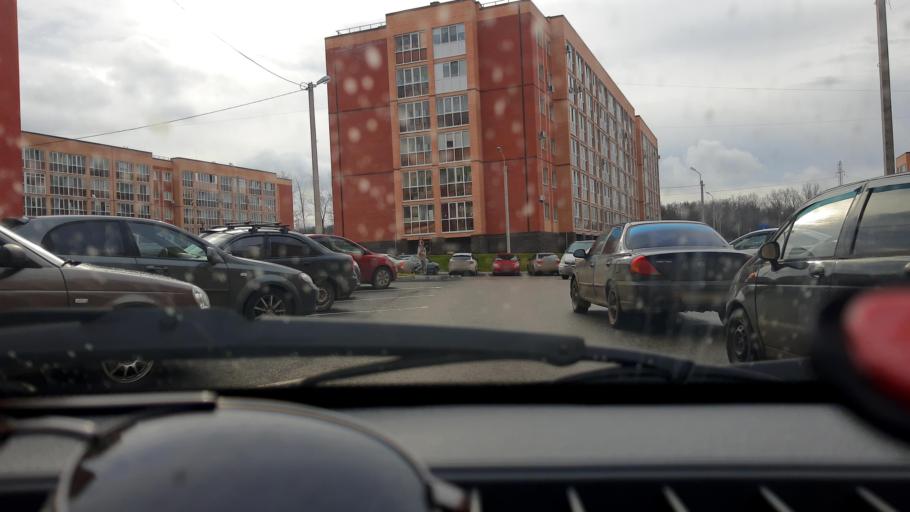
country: RU
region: Bashkortostan
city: Mikhaylovka
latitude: 54.8293
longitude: 55.8613
